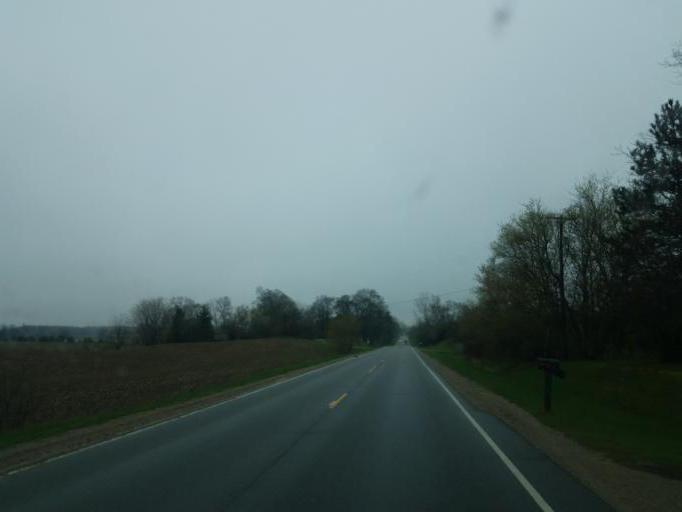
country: US
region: Michigan
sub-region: Isabella County
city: Mount Pleasant
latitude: 43.5239
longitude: -84.8172
